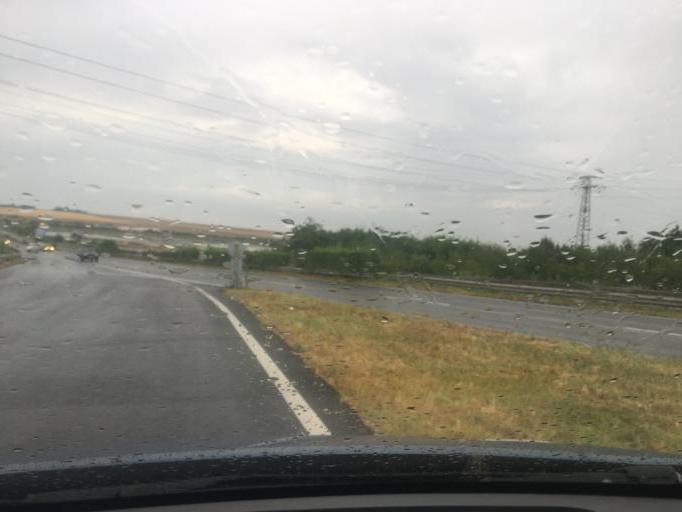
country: BG
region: Burgas
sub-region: Obshtina Burgas
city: Burgas
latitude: 42.5520
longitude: 27.4877
